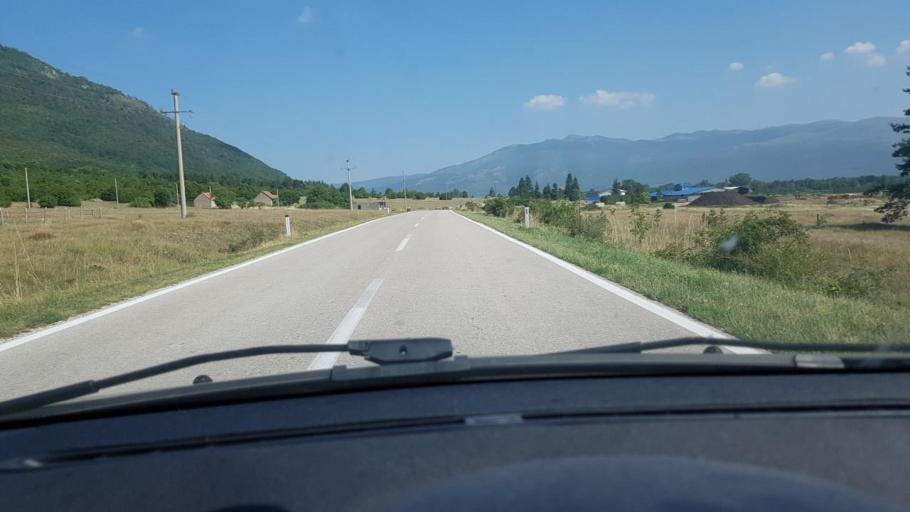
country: BA
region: Federation of Bosnia and Herzegovina
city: Glamoc
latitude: 44.0287
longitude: 16.5967
